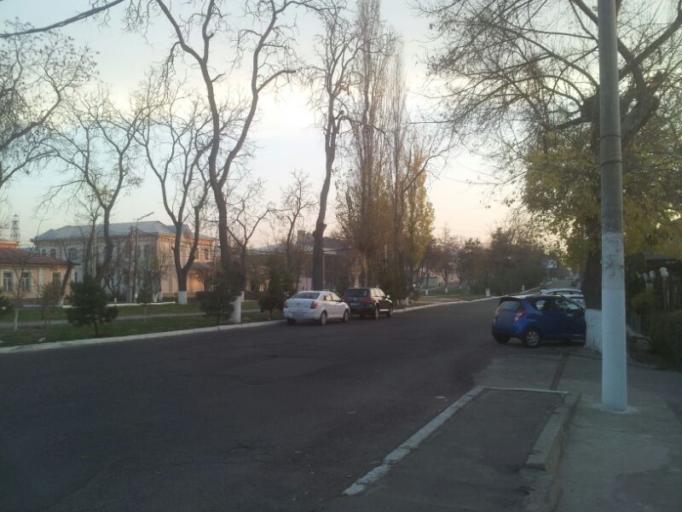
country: UZ
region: Toshkent
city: Salor
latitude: 41.3303
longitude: 69.2915
